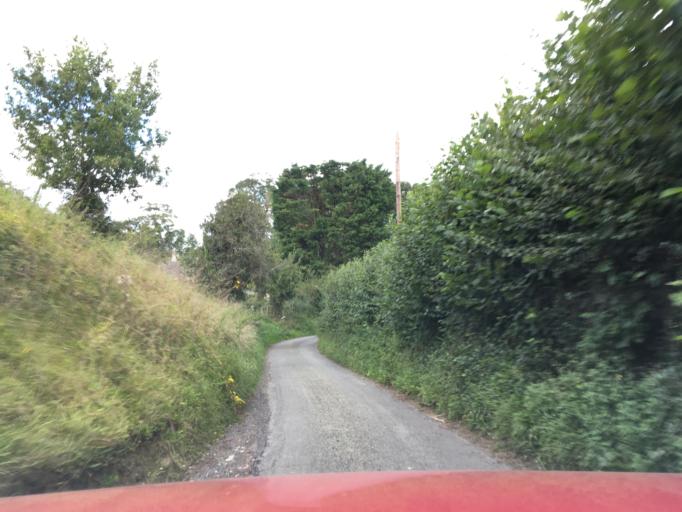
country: GB
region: England
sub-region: Wiltshire
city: Box
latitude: 51.4198
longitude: -2.2589
